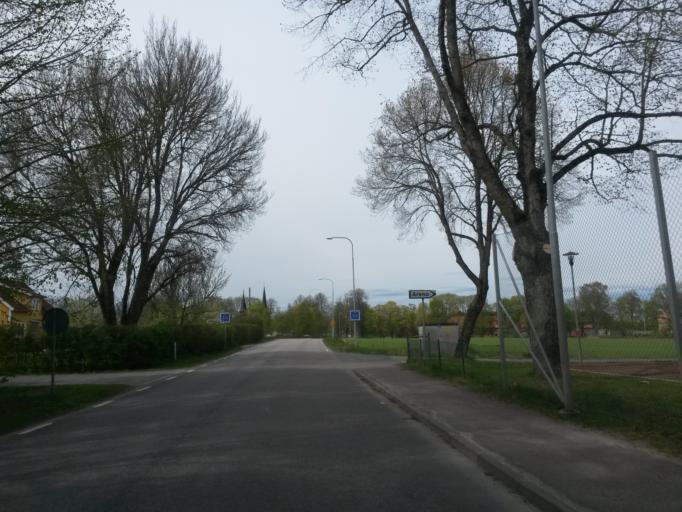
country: SE
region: Vaestra Goetaland
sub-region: Vara Kommun
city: Vara
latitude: 58.3284
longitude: 12.9070
